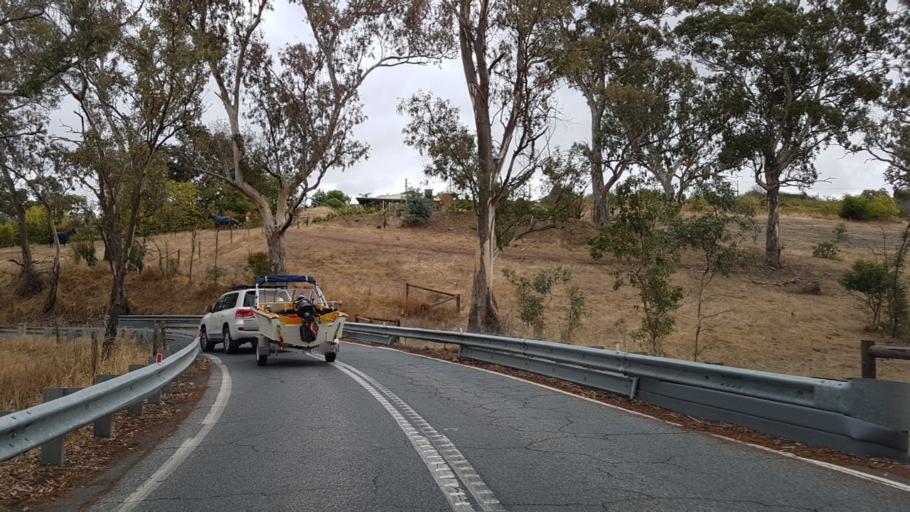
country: AU
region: South Australia
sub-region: Adelaide Hills
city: Gumeracha
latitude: -34.8362
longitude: 138.8212
